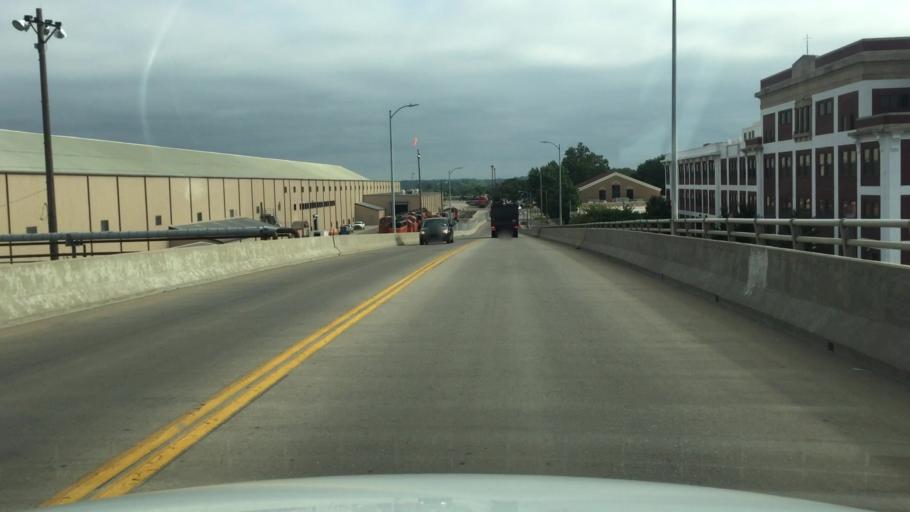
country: US
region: Kansas
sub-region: Shawnee County
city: Topeka
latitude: 39.0557
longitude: -95.6581
